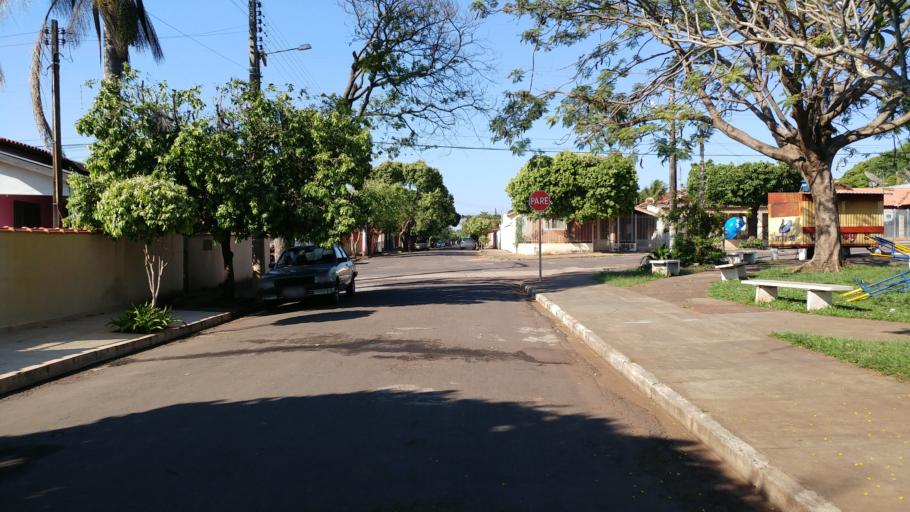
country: BR
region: Sao Paulo
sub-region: Paraguacu Paulista
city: Paraguacu Paulista
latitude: -22.4112
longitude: -50.5687
